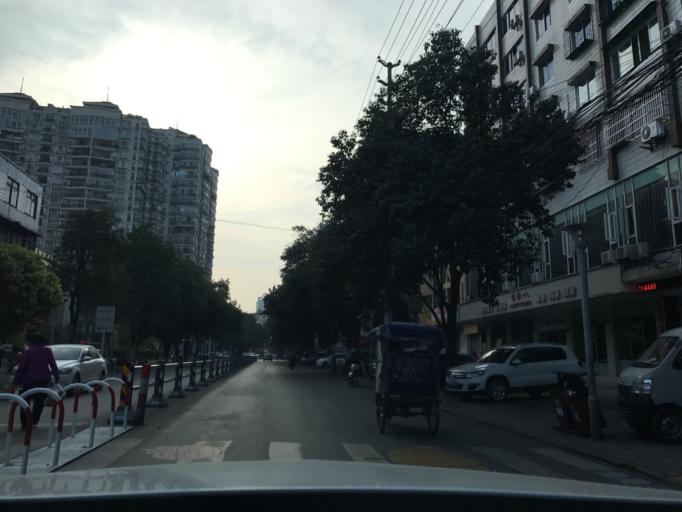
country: CN
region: Sichuan
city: Mianyang
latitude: 31.4546
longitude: 104.7509
